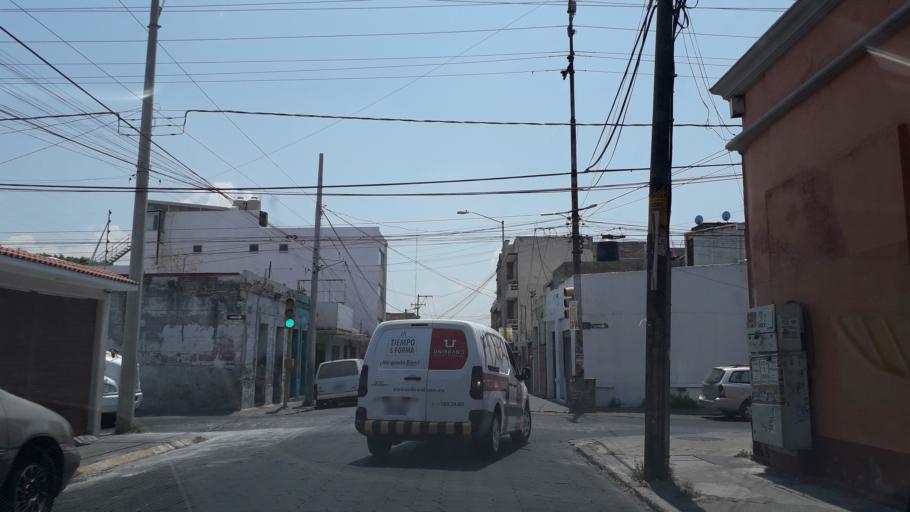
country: MX
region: Puebla
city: Puebla
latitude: 19.0513
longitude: -98.2122
